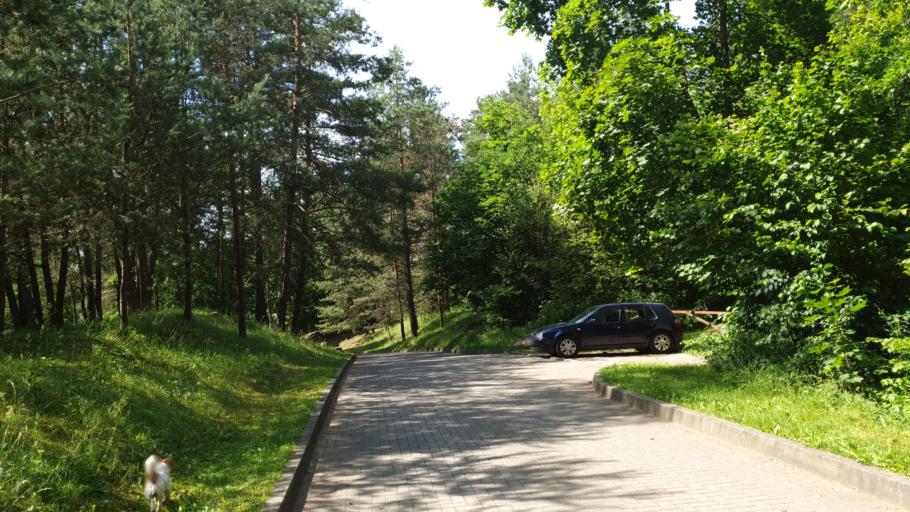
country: LT
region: Vilnius County
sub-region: Vilnius
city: Fabijoniskes
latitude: 54.7936
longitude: 25.2994
